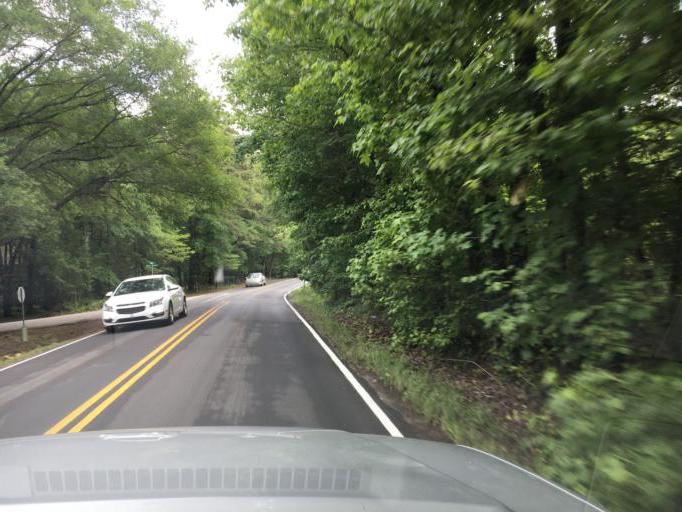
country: US
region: South Carolina
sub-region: Greenville County
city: Taylors
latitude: 34.8549
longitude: -82.2812
